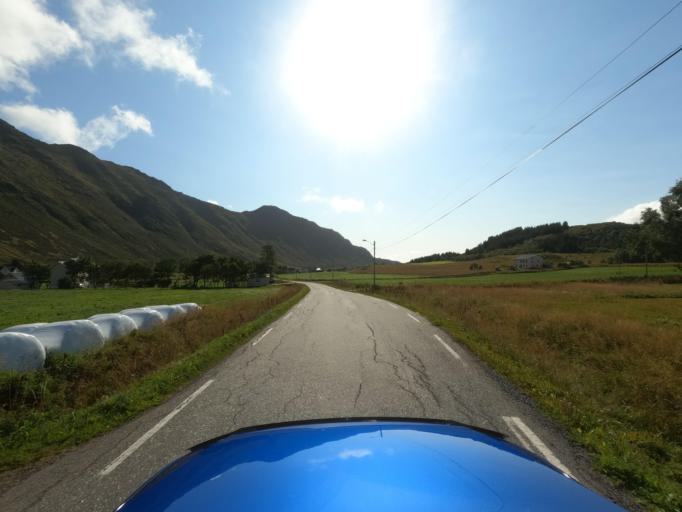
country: NO
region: Nordland
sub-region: Vestvagoy
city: Leknes
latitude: 68.1066
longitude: 13.6537
